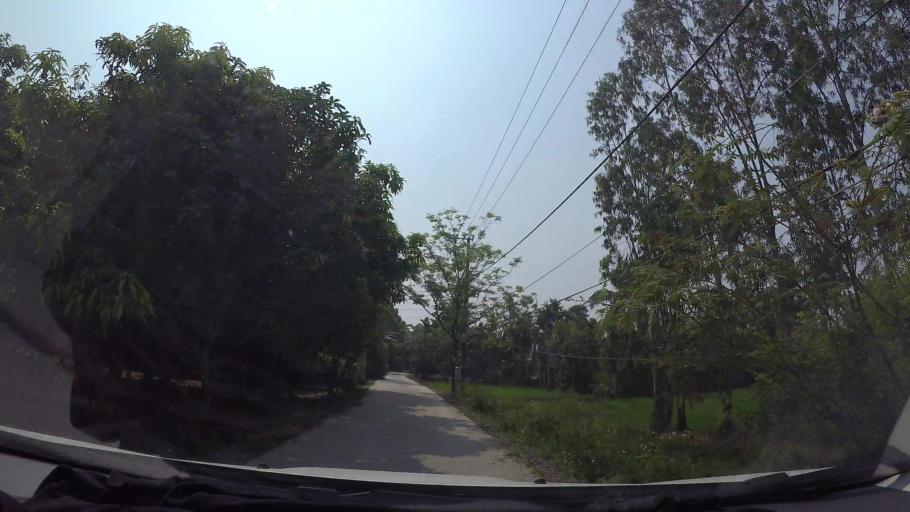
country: VN
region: Da Nang
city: Cam Le
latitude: 15.9776
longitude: 108.2254
